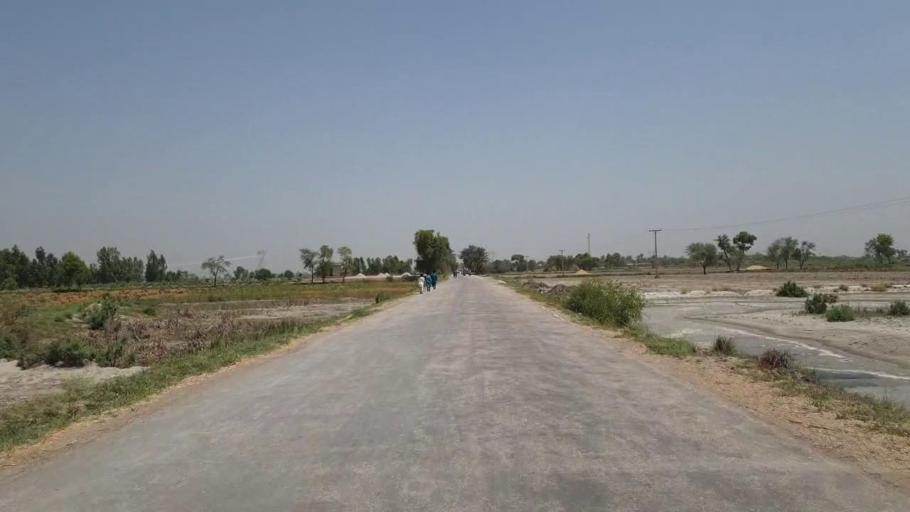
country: PK
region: Sindh
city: Adilpur
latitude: 27.8846
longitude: 69.2878
